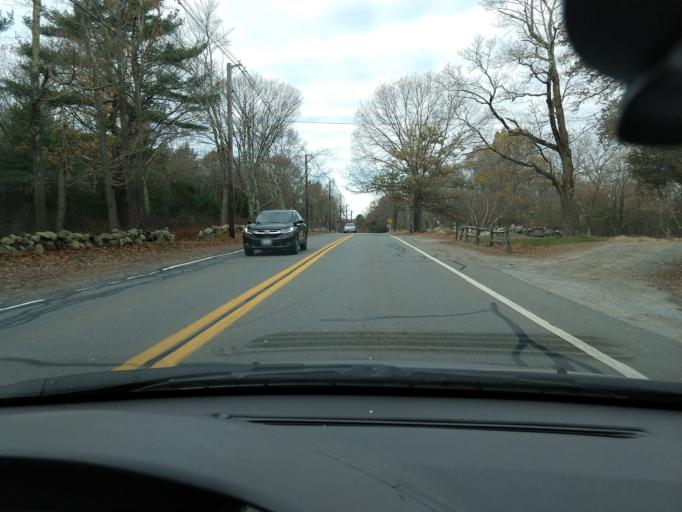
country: US
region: Massachusetts
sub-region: Middlesex County
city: Lincoln
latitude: 42.4489
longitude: -71.2748
